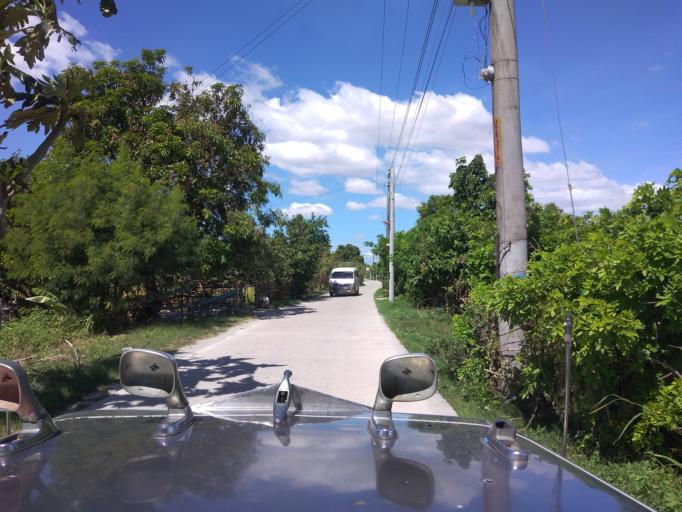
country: PH
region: Central Luzon
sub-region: Province of Pampanga
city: Magliman
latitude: 15.0482
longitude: 120.6424
